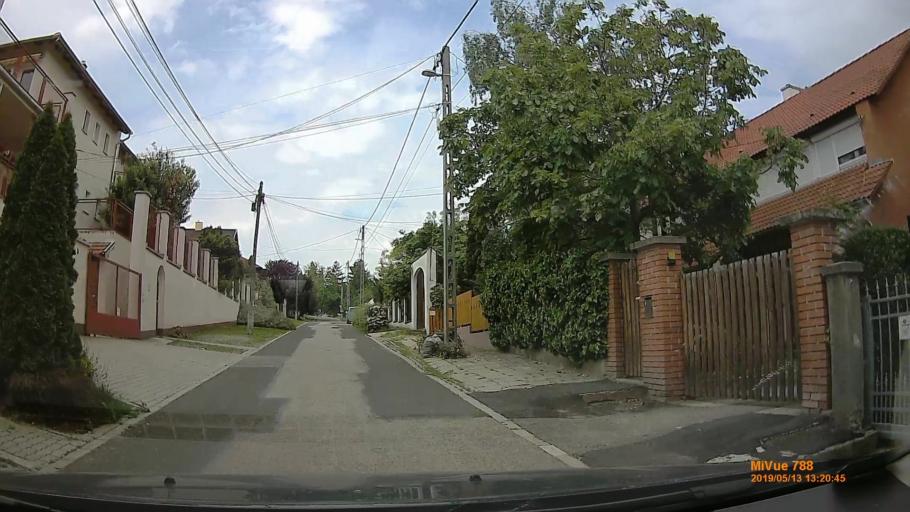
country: HU
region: Budapest
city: Budapest XXII. keruelet
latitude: 47.4118
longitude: 19.0090
